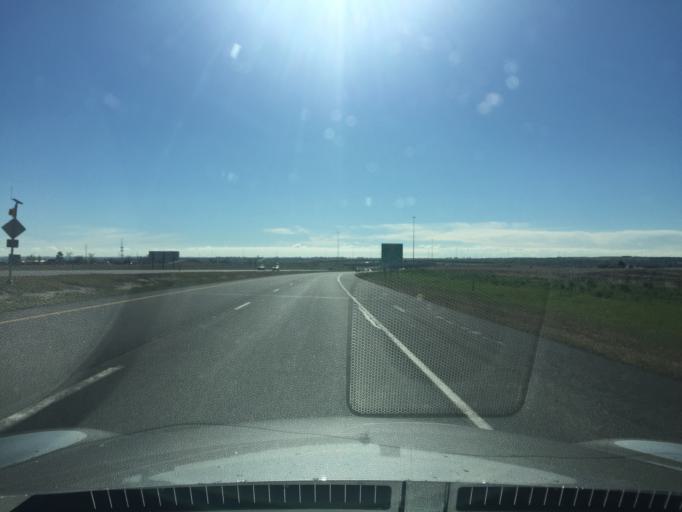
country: US
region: Colorado
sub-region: Boulder County
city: Erie
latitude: 39.9846
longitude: -105.0061
